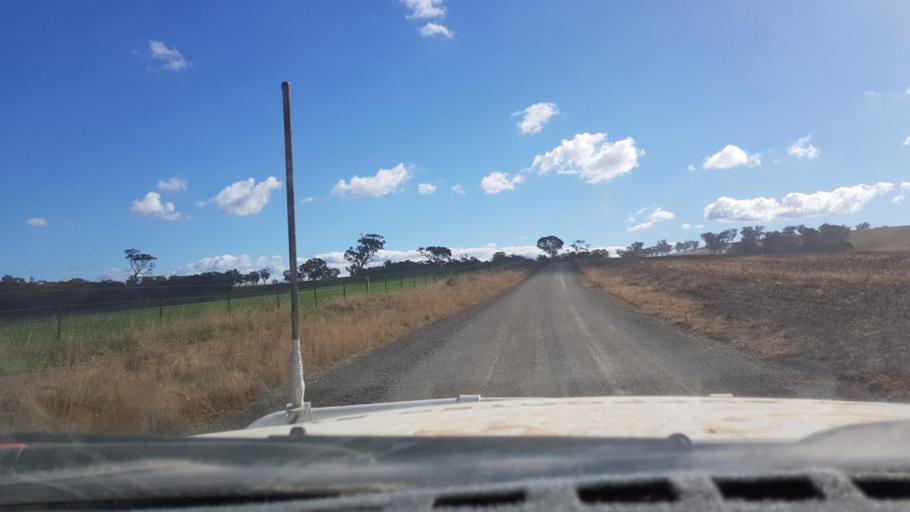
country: AU
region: New South Wales
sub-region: Narrabri
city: Blair Athol
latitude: -30.5580
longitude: 150.4621
